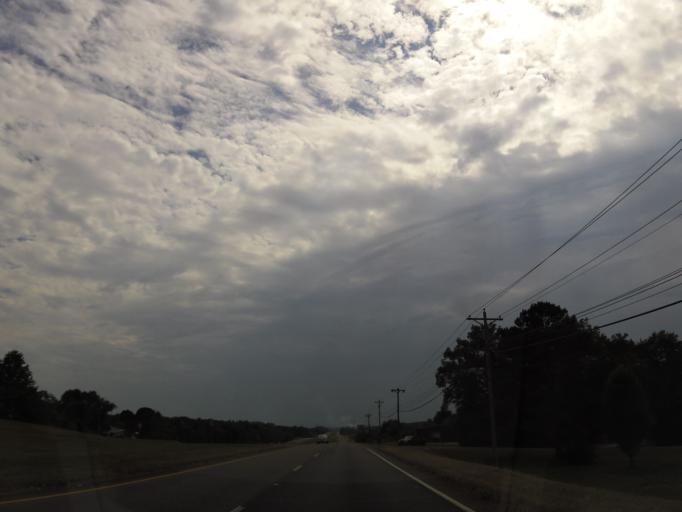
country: US
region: Alabama
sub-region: Jackson County
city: Scottsboro
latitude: 34.7390
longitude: -85.9273
